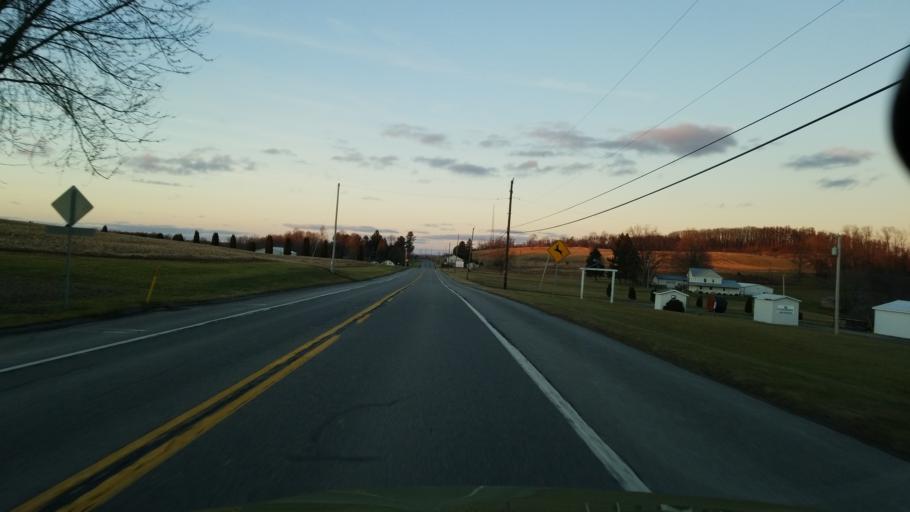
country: US
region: Pennsylvania
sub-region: Jefferson County
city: Punxsutawney
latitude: 40.8664
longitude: -79.0204
